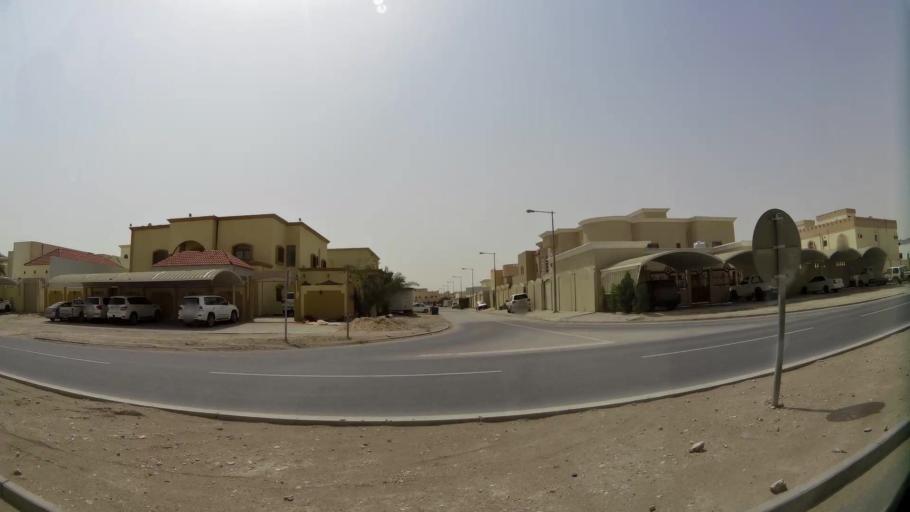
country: QA
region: Baladiyat ar Rayyan
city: Ar Rayyan
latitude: 25.2478
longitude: 51.3772
